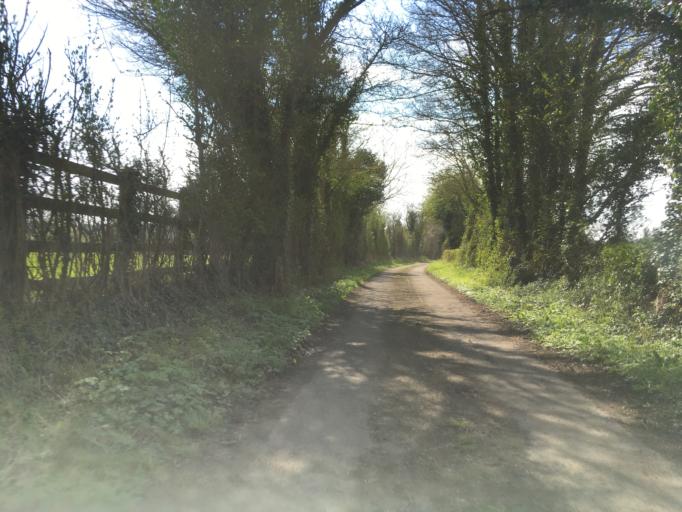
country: GB
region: England
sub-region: South Gloucestershire
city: Almondsbury
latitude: 51.5666
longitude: -2.5783
